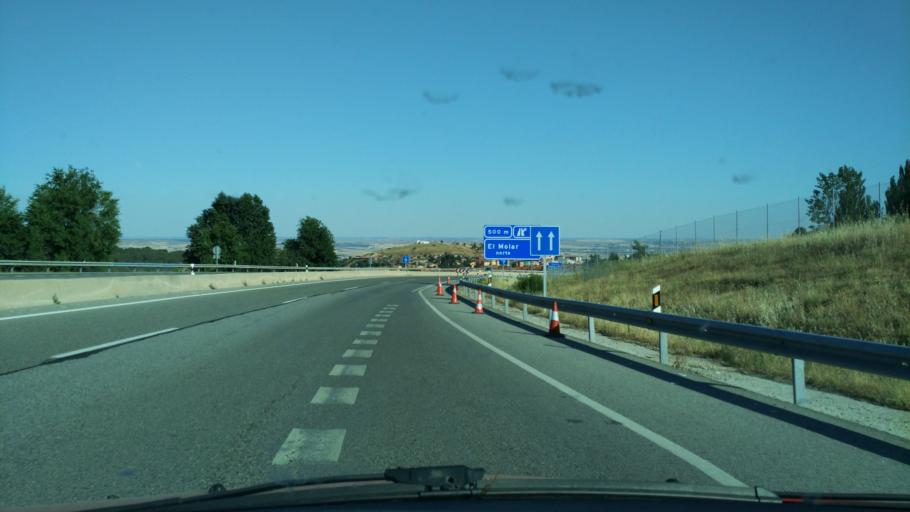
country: ES
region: Madrid
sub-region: Provincia de Madrid
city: Pedrezuela
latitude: 40.7432
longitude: -3.5897
